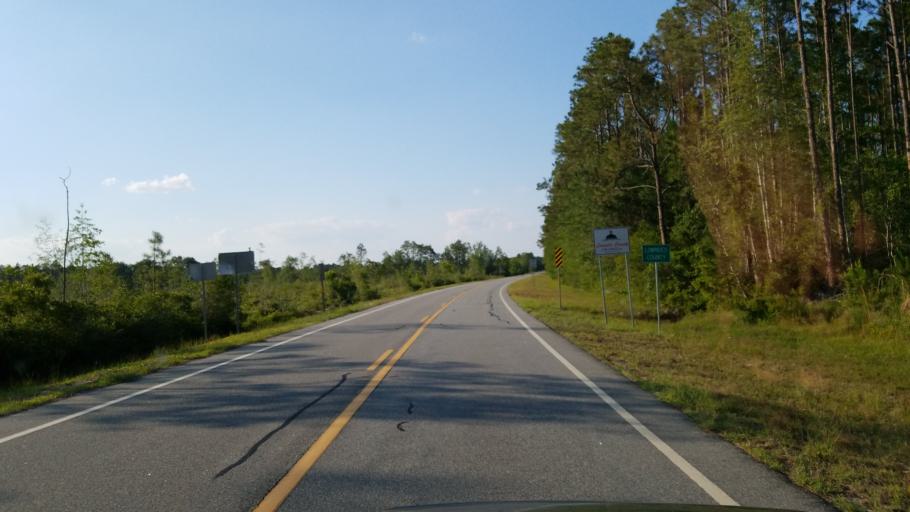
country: US
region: Georgia
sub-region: Echols County
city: Statenville
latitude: 30.8483
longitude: -83.0530
